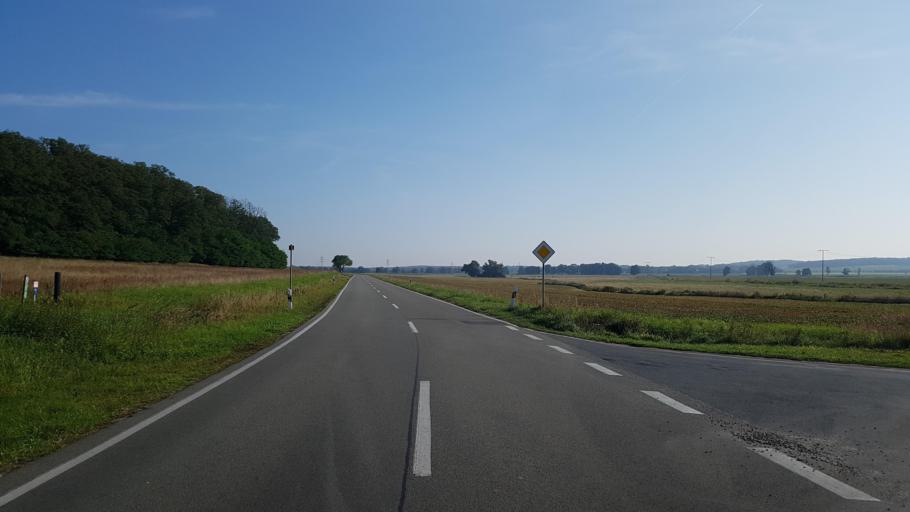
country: DE
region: Brandenburg
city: Pawesin
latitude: 52.5021
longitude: 12.6268
